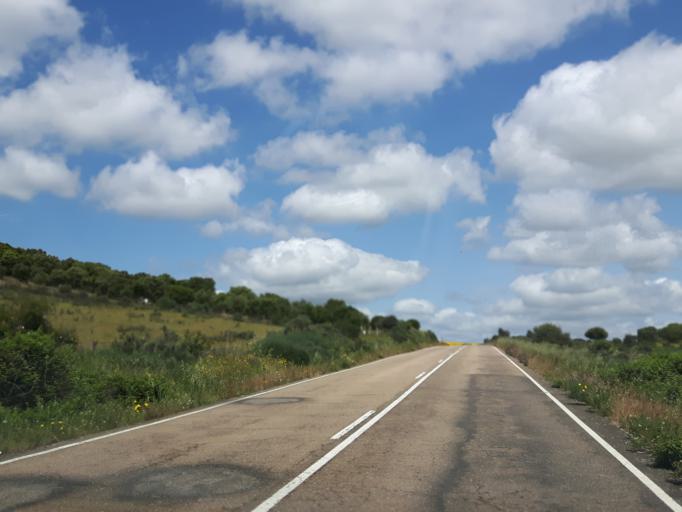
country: ES
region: Castille and Leon
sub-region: Provincia de Salamanca
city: Villar de la Yegua
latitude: 40.7100
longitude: -6.6808
